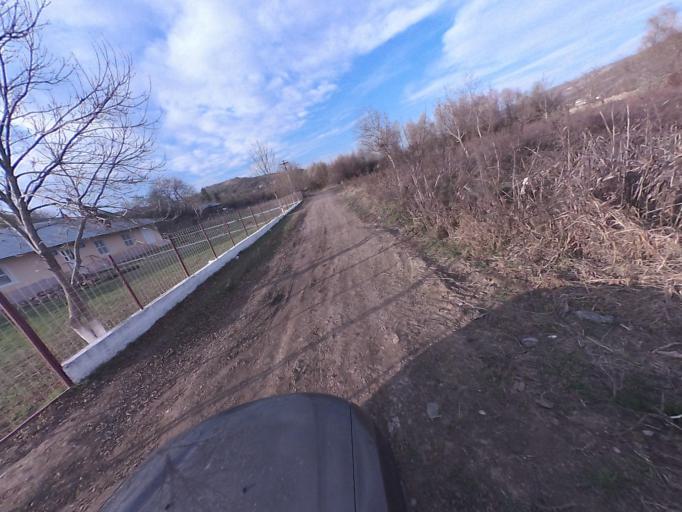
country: RO
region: Vaslui
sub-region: Comuna Gherghesti
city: Gherghesti
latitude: 46.4883
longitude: 27.5298
